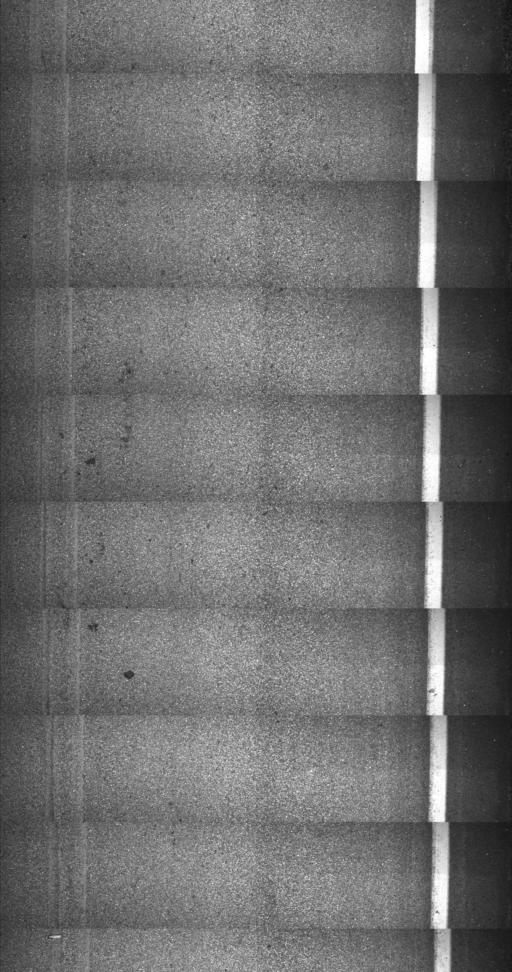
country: US
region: Vermont
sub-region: Rutland County
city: Poultney
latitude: 43.5105
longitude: -73.2183
